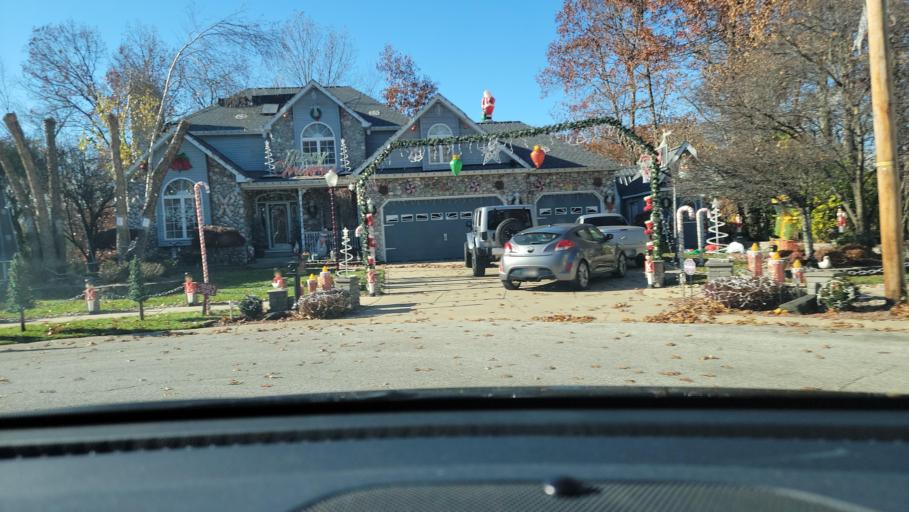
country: US
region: Indiana
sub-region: Porter County
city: Portage
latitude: 41.5898
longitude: -87.1442
